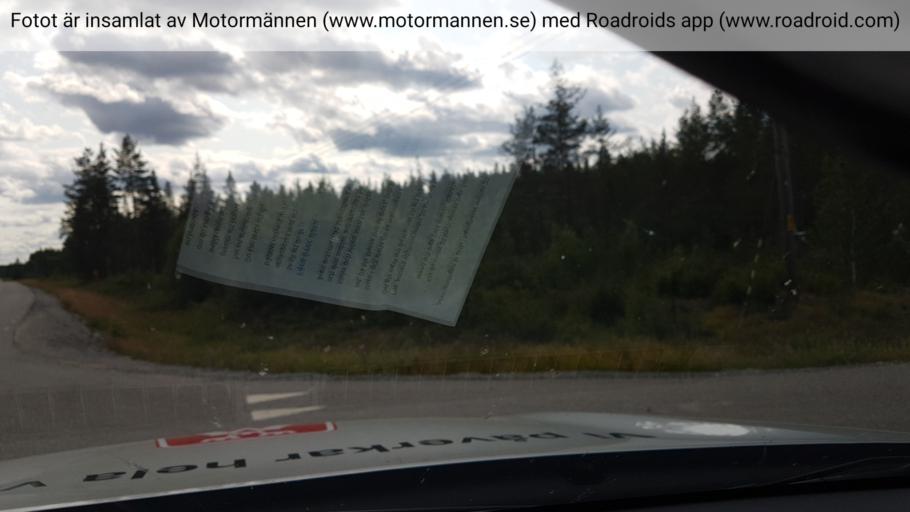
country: SE
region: Vaesterbotten
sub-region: Skelleftea Kommun
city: Boliden
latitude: 65.2921
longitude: 20.2201
